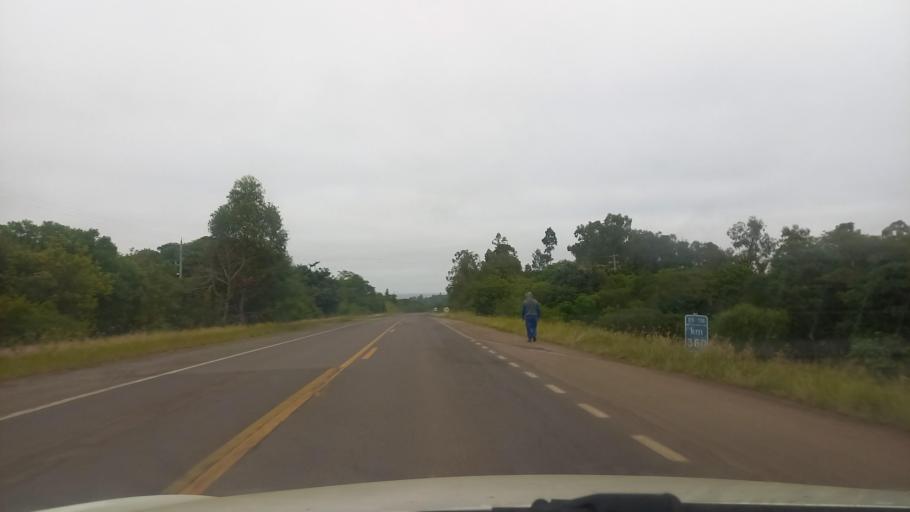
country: BR
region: Rio Grande do Sul
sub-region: Sao Pedro Do Sul
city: Sao Pedro do Sul
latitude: -29.7752
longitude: -54.0983
